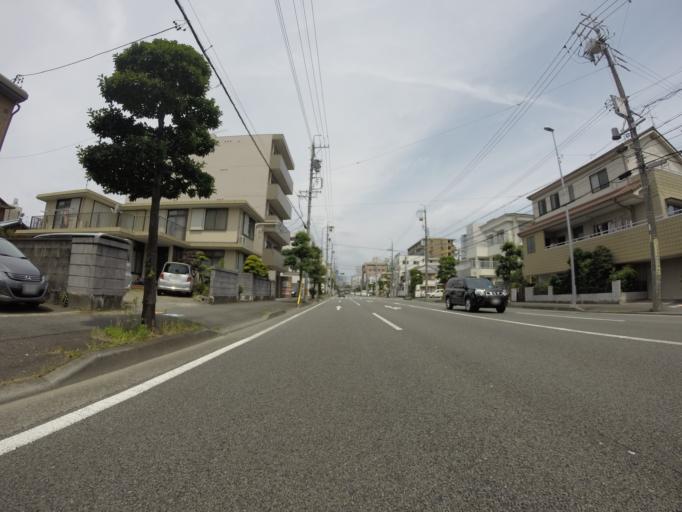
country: JP
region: Shizuoka
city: Shizuoka-shi
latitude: 34.9667
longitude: 138.3890
